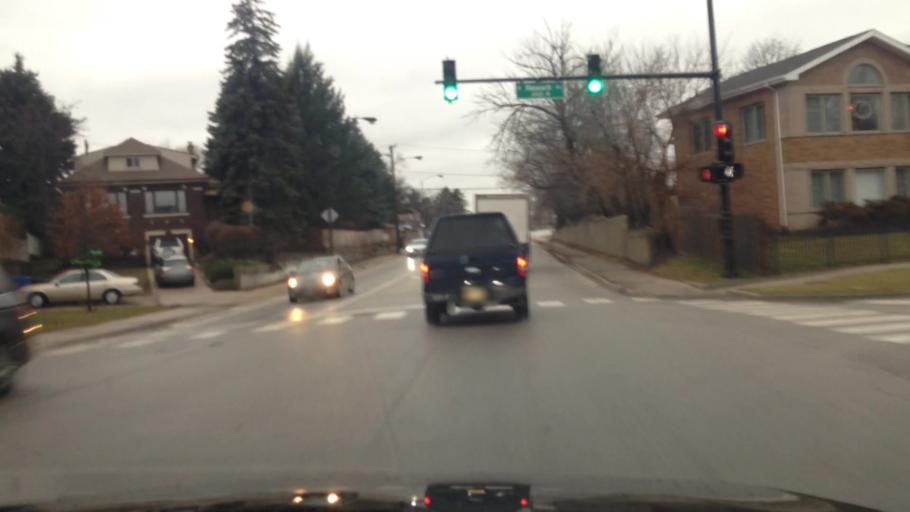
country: US
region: Illinois
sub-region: Cook County
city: Niles
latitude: 41.9968
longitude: -87.7987
